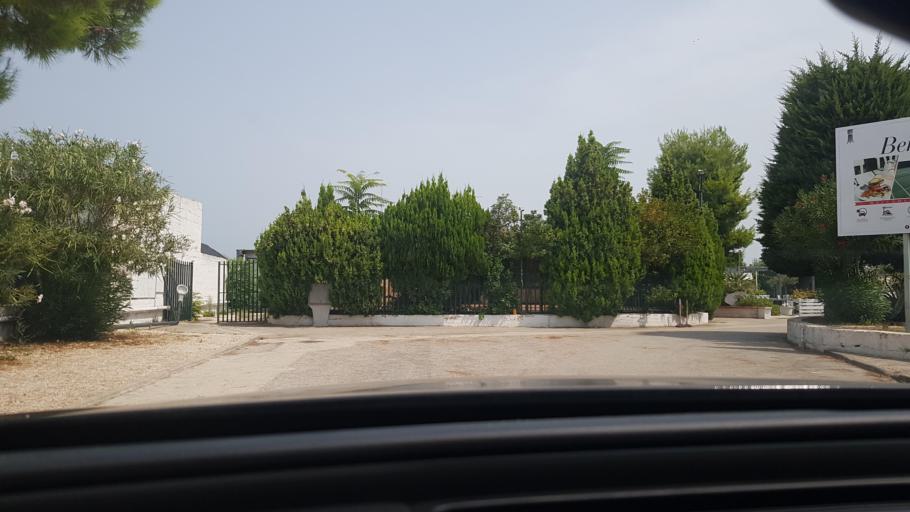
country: IT
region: Apulia
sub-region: Provincia di Barletta - Andria - Trani
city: Andria
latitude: 41.2317
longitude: 16.2751
